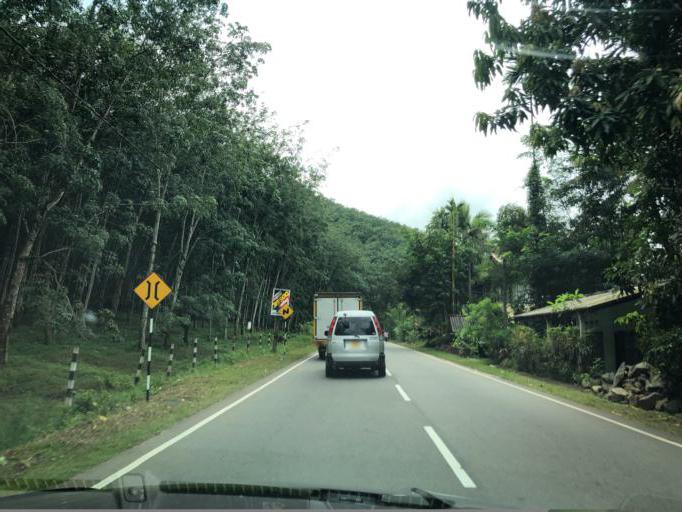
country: LK
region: Western
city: Horana South
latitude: 6.6807
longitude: 80.1473
